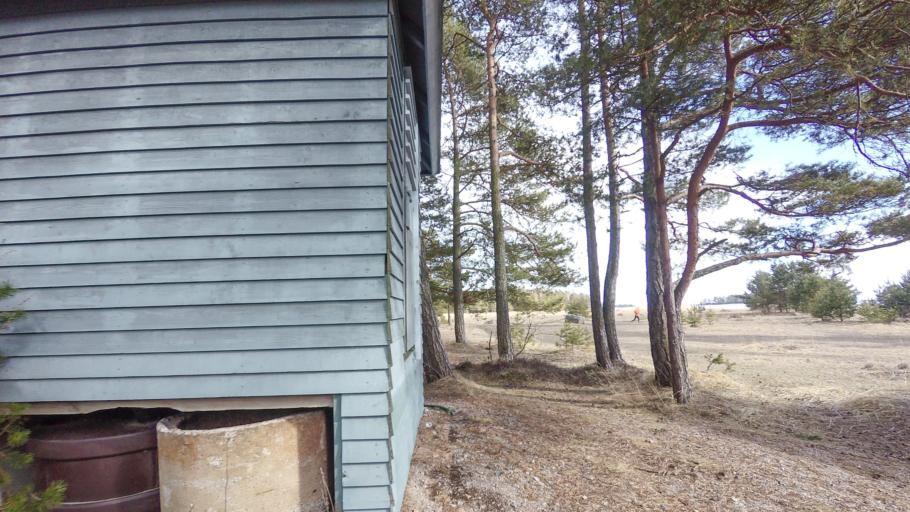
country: FI
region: Uusimaa
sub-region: Helsinki
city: Vantaa
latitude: 60.1871
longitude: 25.1448
